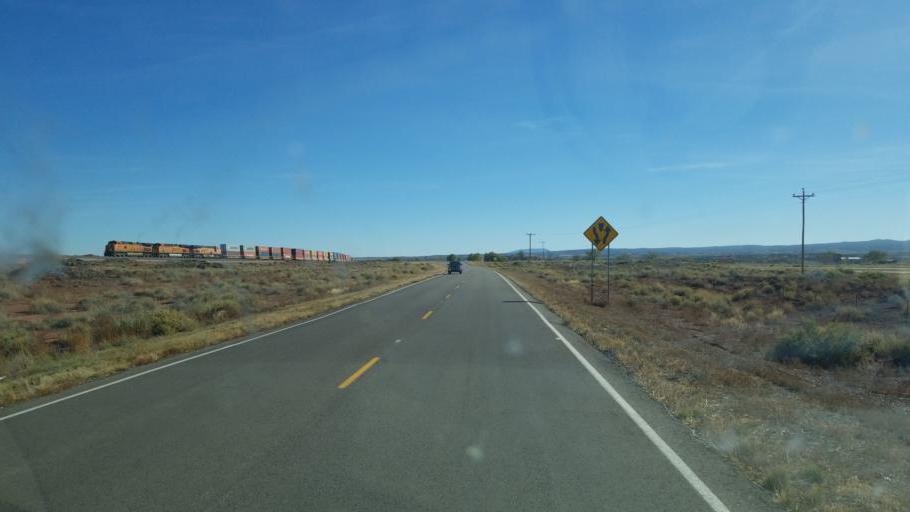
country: US
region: New Mexico
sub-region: Cibola County
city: Milan
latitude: 35.2879
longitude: -107.9859
